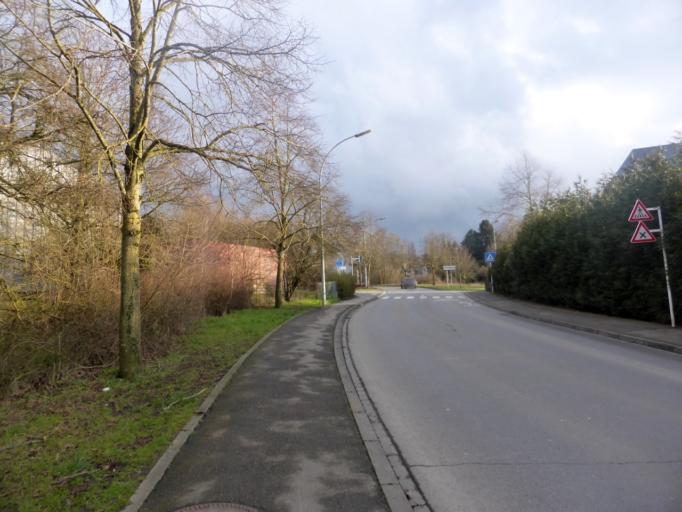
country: LU
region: Luxembourg
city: Belvaux
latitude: 49.5159
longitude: 5.9266
